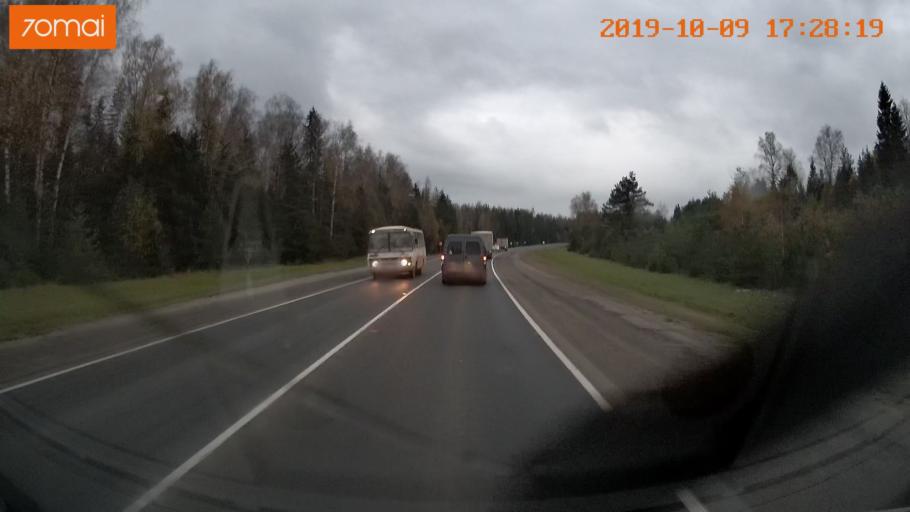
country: RU
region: Ivanovo
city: Furmanov
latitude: 57.1588
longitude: 41.0687
